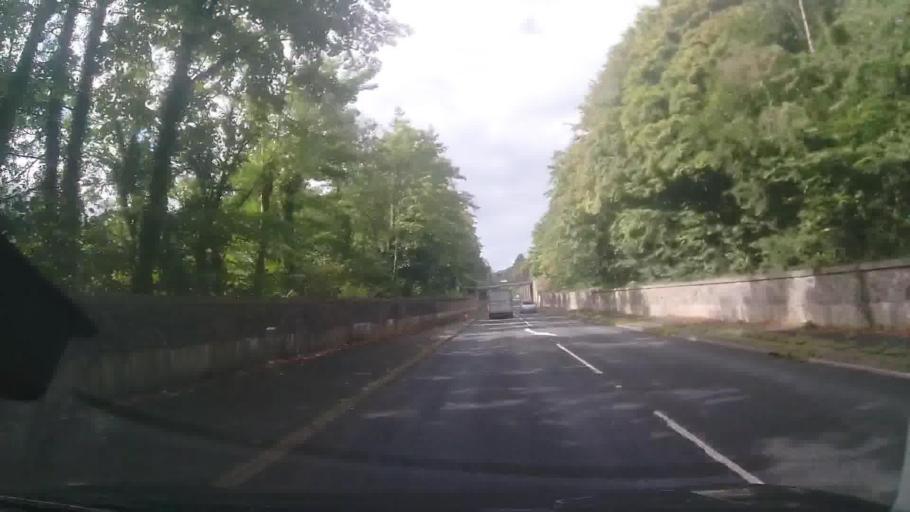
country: GB
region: Wales
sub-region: Gwynedd
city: Dolgellau
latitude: 52.7449
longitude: -3.8818
